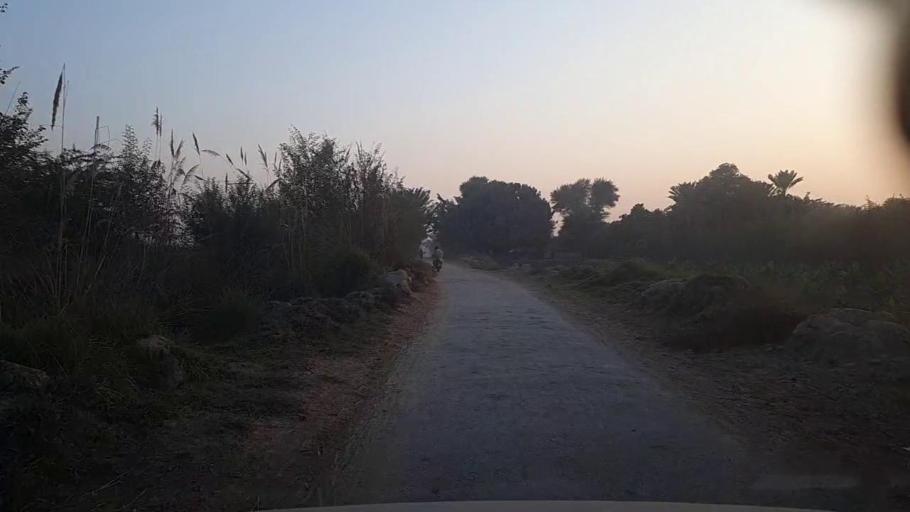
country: PK
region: Sindh
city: Karaundi
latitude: 26.8453
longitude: 68.3712
